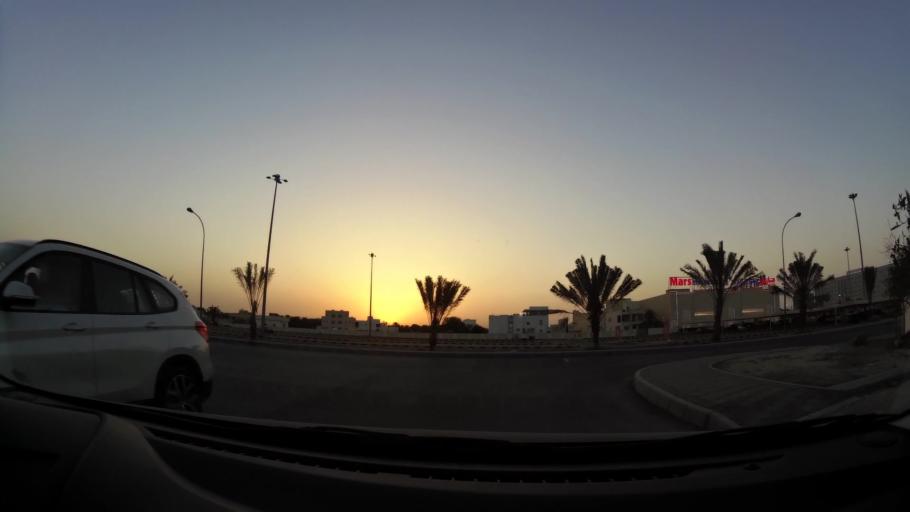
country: OM
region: Muhafazat Masqat
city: As Sib al Jadidah
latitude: 23.6477
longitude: 58.2152
